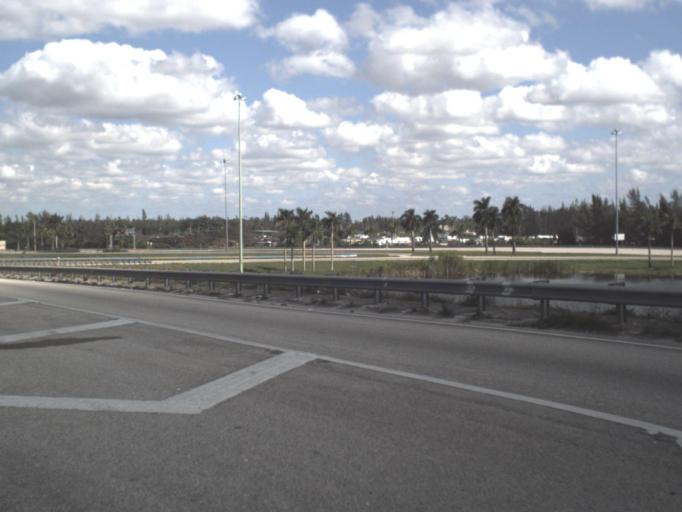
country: US
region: Florida
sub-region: Miami-Dade County
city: Palm Springs North
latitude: 25.9010
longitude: -80.3851
